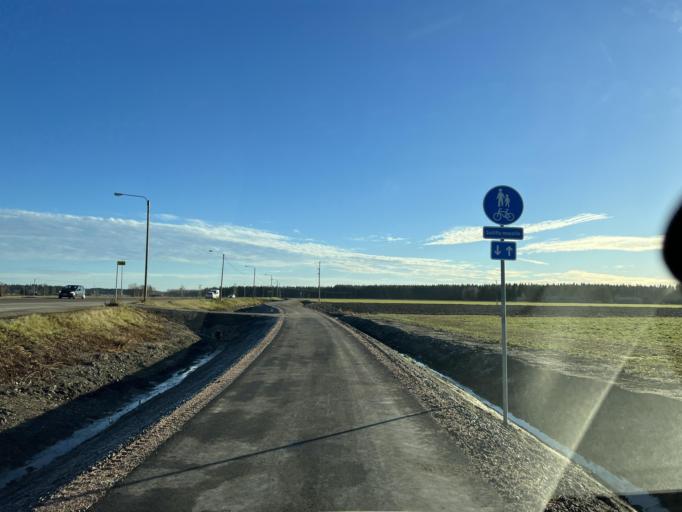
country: FI
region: Northern Ostrobothnia
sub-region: Nivala-Haapajaervi
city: Nivala
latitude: 63.9533
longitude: 24.8708
